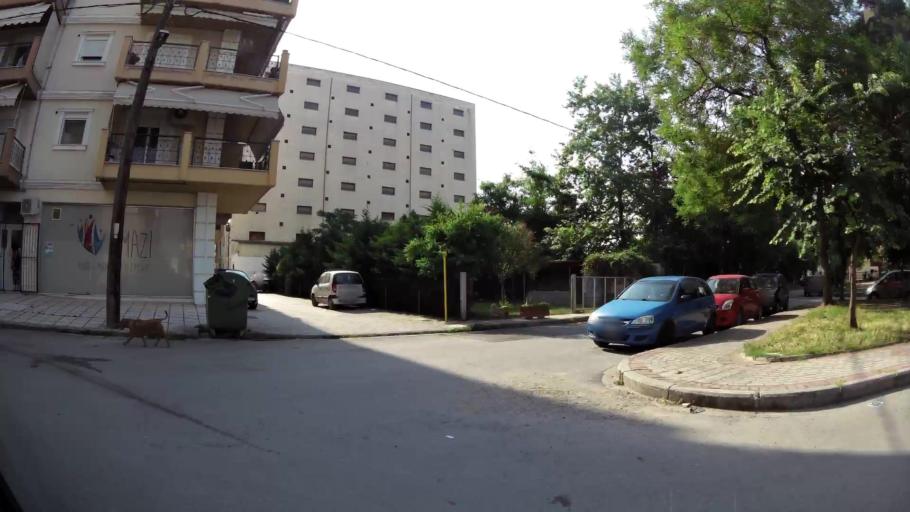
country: GR
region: Central Macedonia
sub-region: Nomos Thessalonikis
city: Ampelokipoi
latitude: 40.6638
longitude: 22.9203
